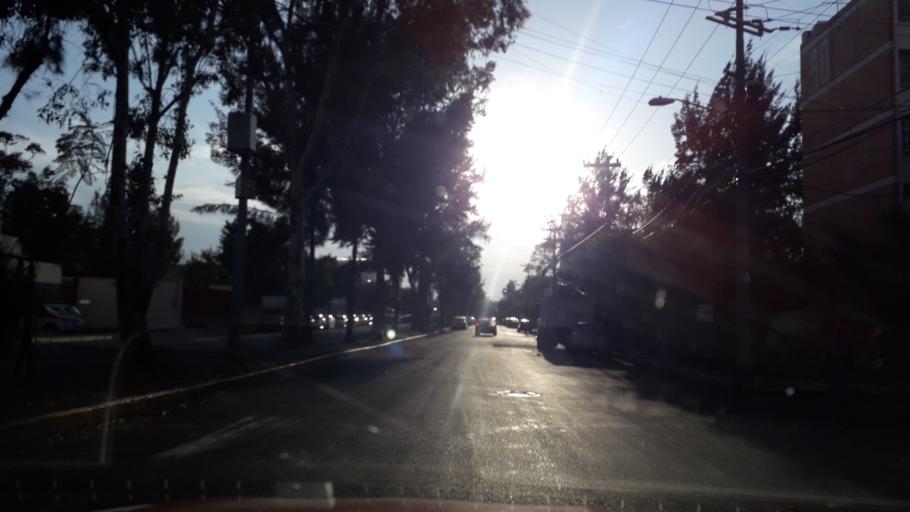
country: MX
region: Mexico City
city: Iztapalapa
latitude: 19.3584
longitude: -99.0503
